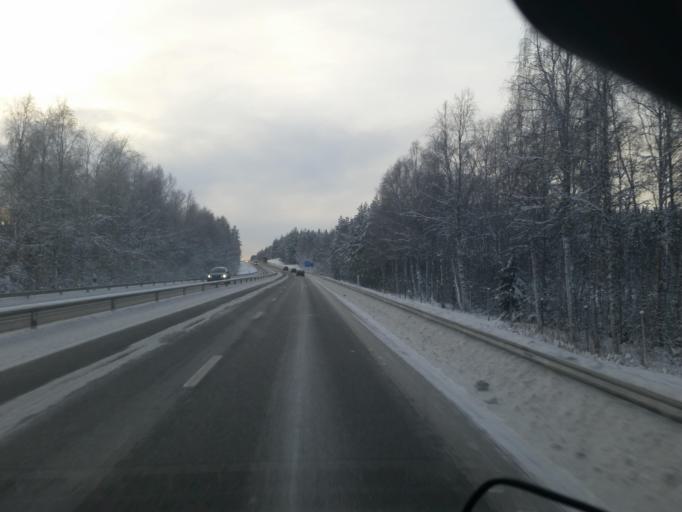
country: SE
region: Norrbotten
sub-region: Pitea Kommun
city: Norrfjarden
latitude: 65.3869
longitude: 21.4420
